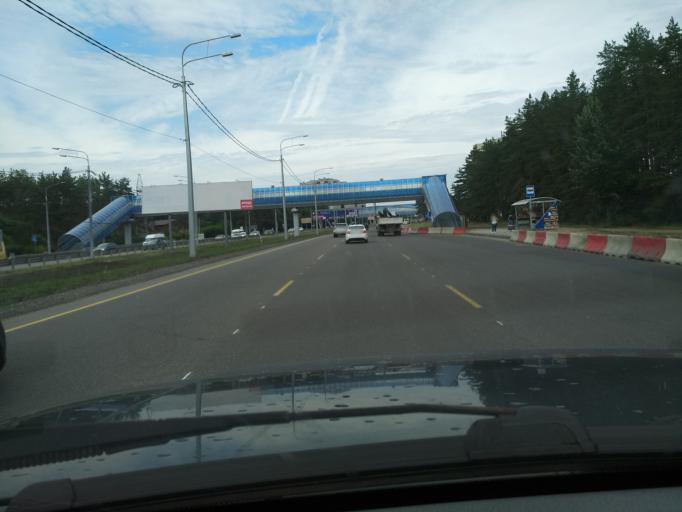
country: RU
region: Voronezj
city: Podgornoye
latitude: 51.7276
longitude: 39.1790
